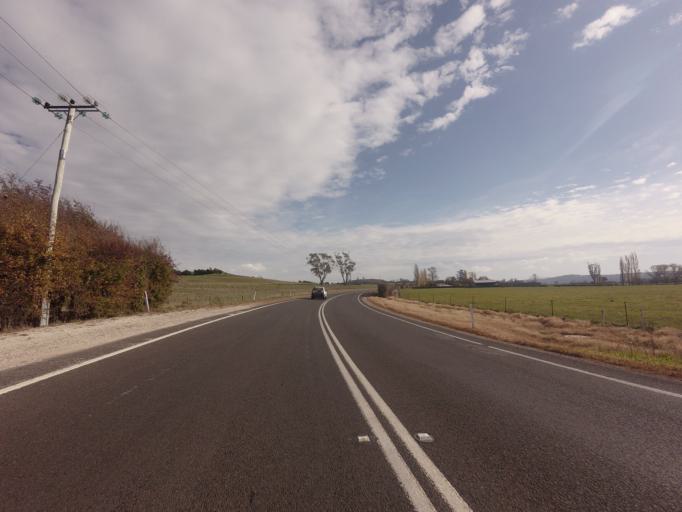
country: AU
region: Tasmania
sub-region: Meander Valley
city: Westbury
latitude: -41.5274
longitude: 146.7609
